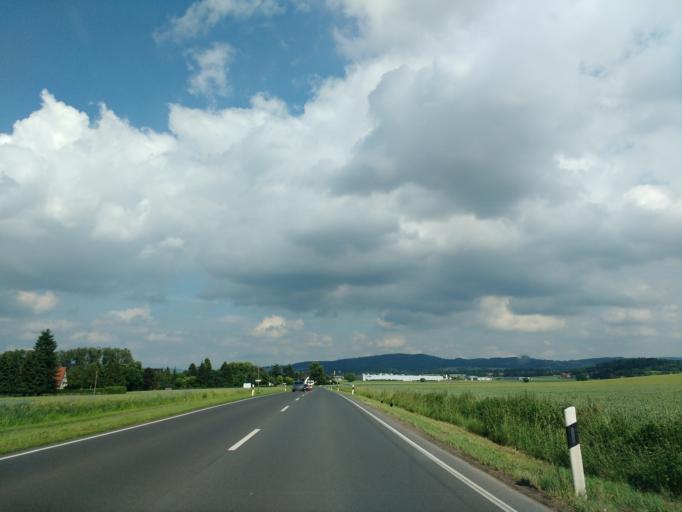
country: DE
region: Lower Saxony
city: Rinteln
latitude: 52.1658
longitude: 9.0527
